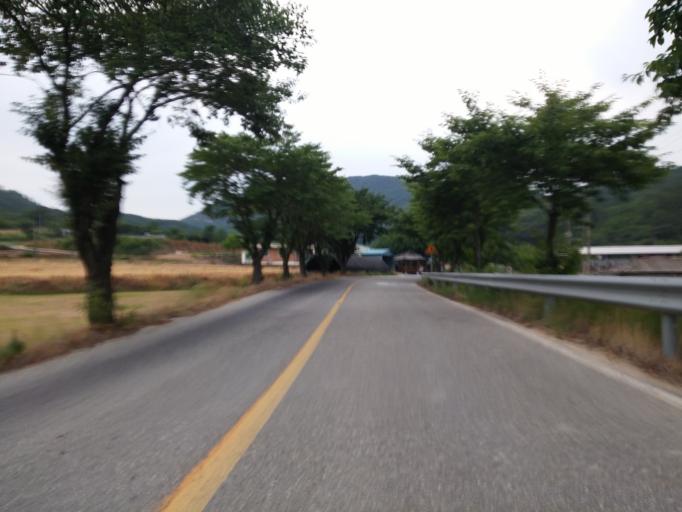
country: KR
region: Chungcheongbuk-do
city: Okcheon
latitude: 36.1947
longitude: 127.5547
